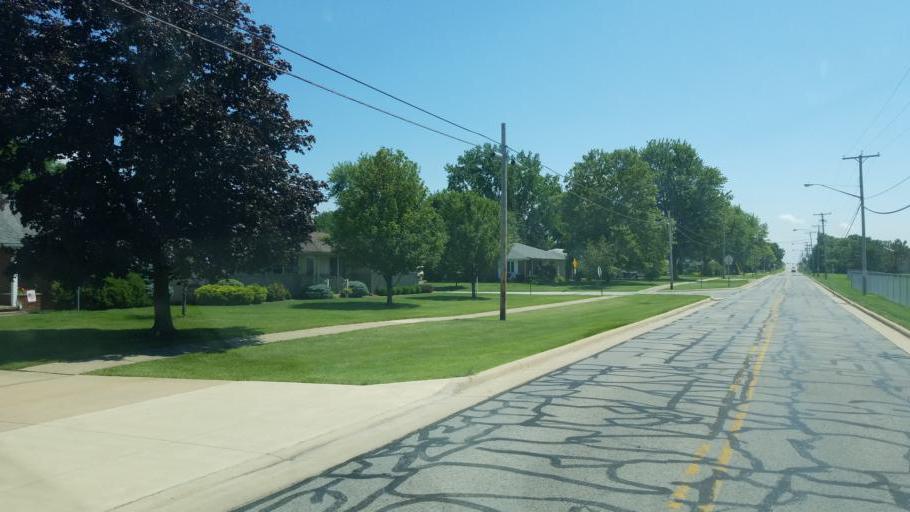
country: US
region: Ohio
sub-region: Ottawa County
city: Port Clinton
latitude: 41.5052
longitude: -82.9338
